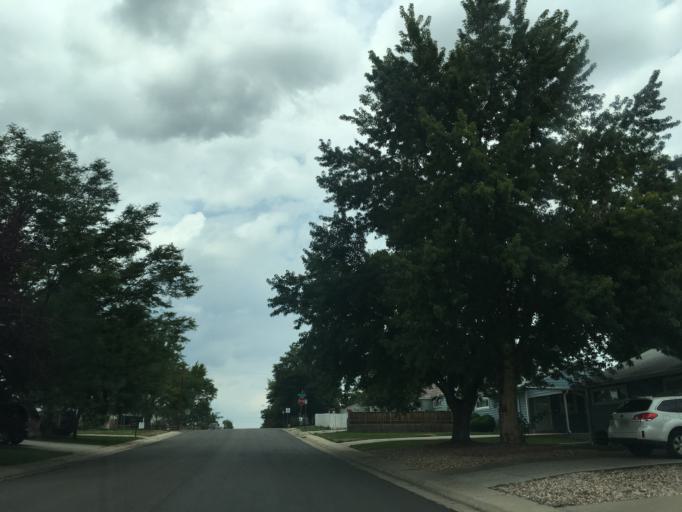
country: US
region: Colorado
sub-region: Arapahoe County
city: Sheridan
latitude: 39.6834
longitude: -105.0148
